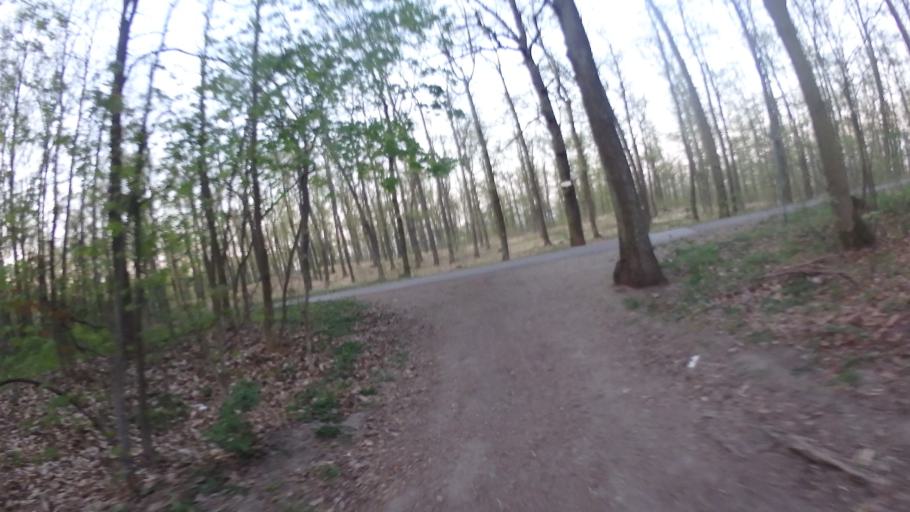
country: CZ
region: South Moravian
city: Ostopovice
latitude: 49.1861
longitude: 16.5536
